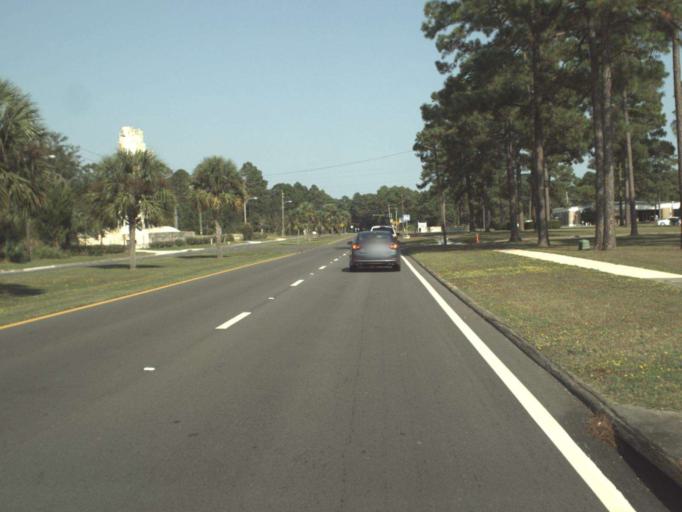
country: US
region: Florida
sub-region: Gulf County
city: Port Saint Joe
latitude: 29.8151
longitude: -85.2918
